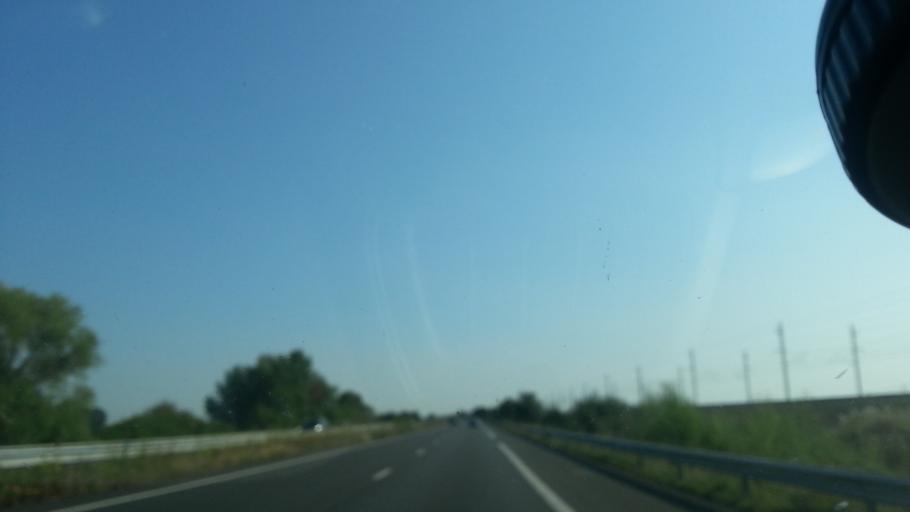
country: FR
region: Centre
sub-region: Departement d'Indre-et-Loire
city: La Celle-Saint-Avant
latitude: 47.0398
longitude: 0.5788
